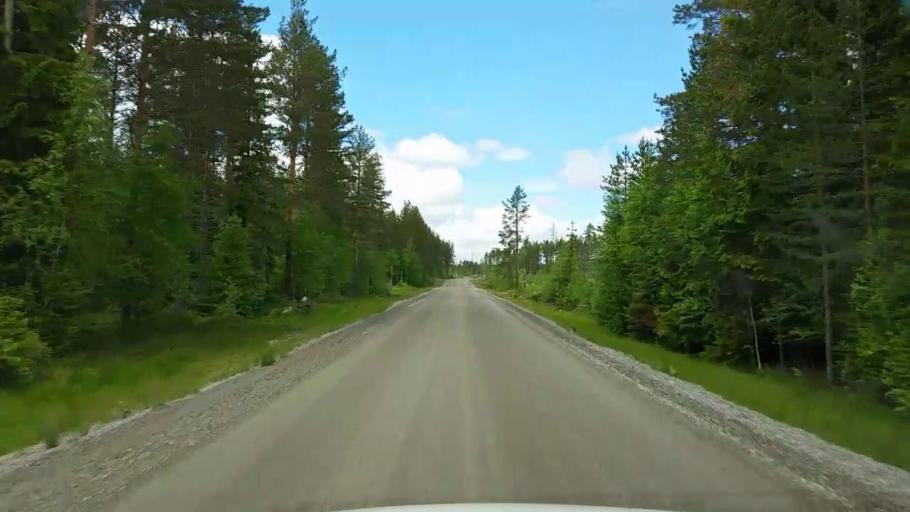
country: SE
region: Gaevleborg
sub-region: Bollnas Kommun
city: Kilafors
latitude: 61.0010
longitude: 16.3916
